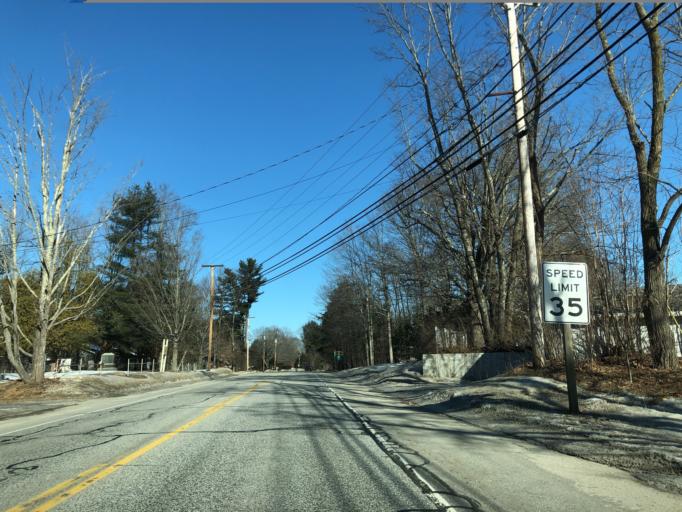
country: US
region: Maine
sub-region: Cumberland County
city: North Windham
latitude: 43.7985
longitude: -70.4075
